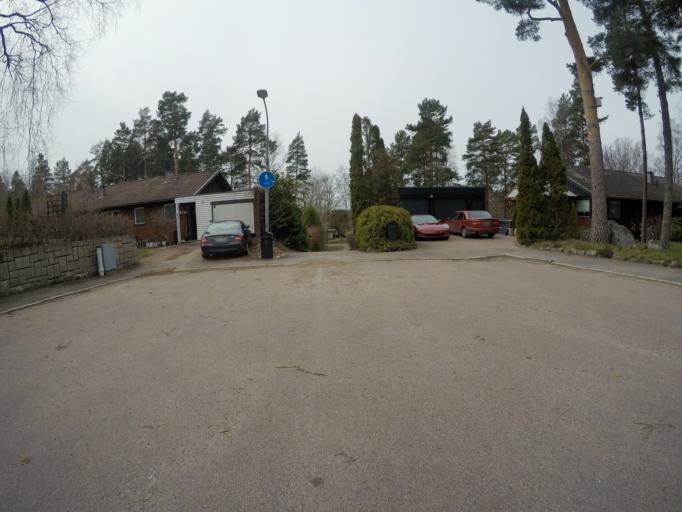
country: SE
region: Vaestmanland
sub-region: Vasteras
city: Vasteras
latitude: 59.5949
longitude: 16.6070
